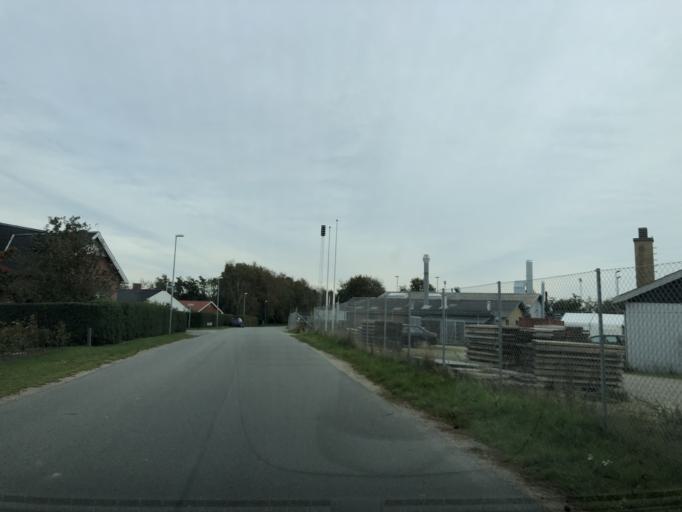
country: DK
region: Central Jutland
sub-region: Syddjurs Kommune
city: Hornslet
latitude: 56.3080
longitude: 10.3102
